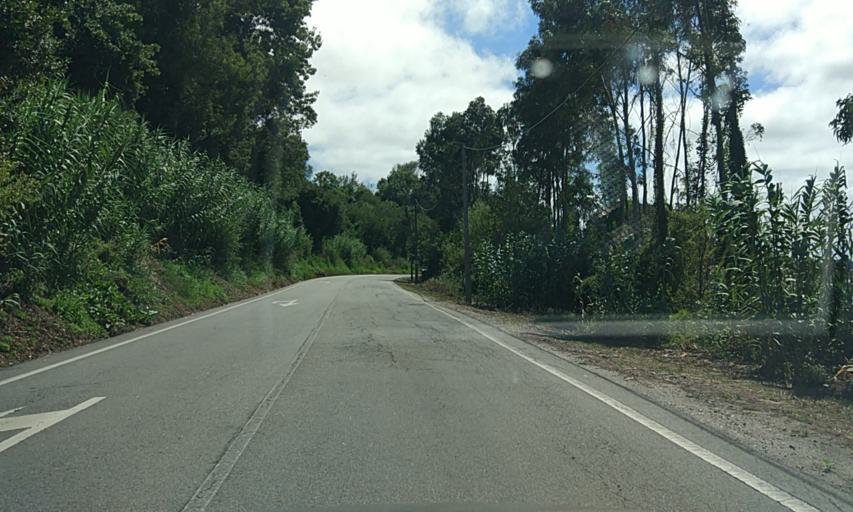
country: PT
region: Aveiro
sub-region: Vagos
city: Vagos
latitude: 40.5795
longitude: -8.6811
